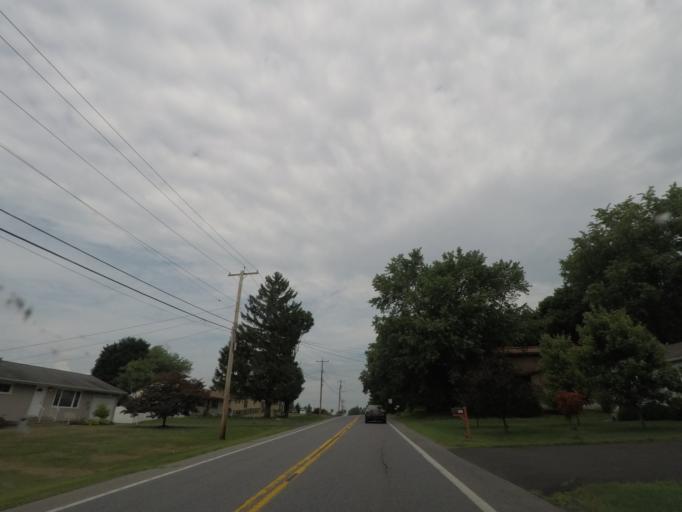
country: US
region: New York
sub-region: Saratoga County
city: Waterford
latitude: 42.8206
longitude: -73.7029
